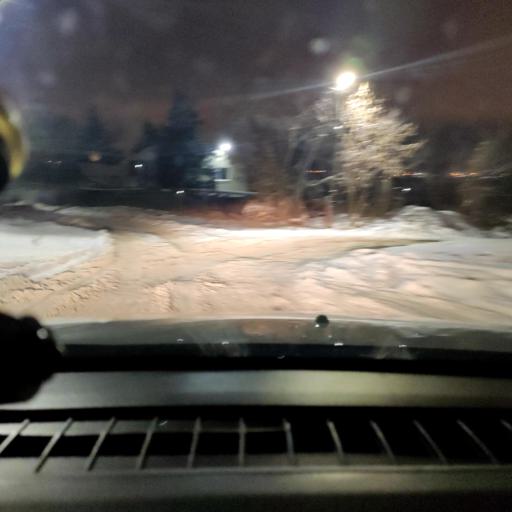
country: RU
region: Samara
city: Samara
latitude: 53.1731
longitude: 50.1683
